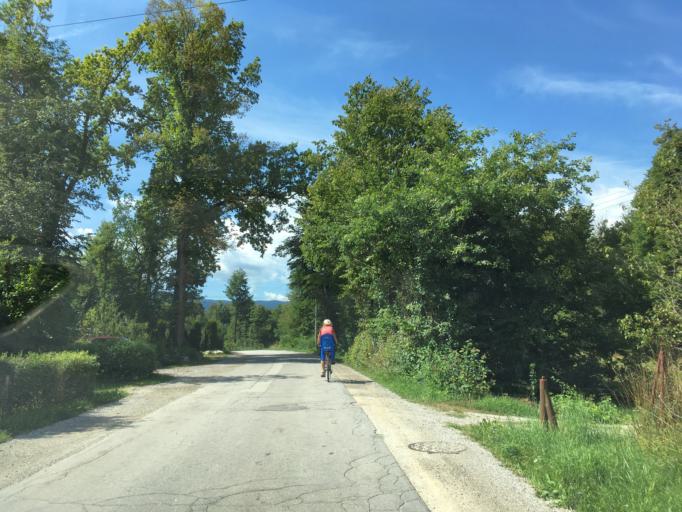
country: SI
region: Radovljica
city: Lesce
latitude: 46.3775
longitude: 14.1708
